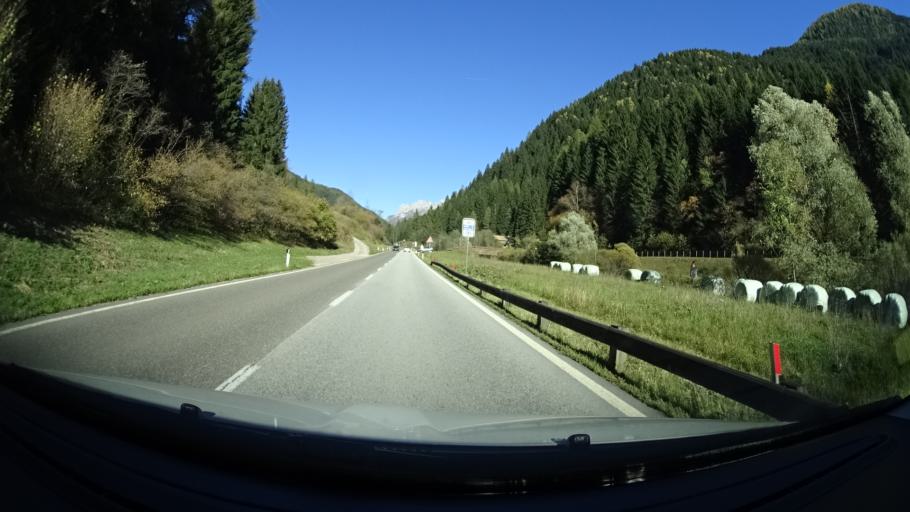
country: IT
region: Trentino-Alto Adige
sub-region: Provincia di Trento
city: Predazzo
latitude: 46.3308
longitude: 11.6024
